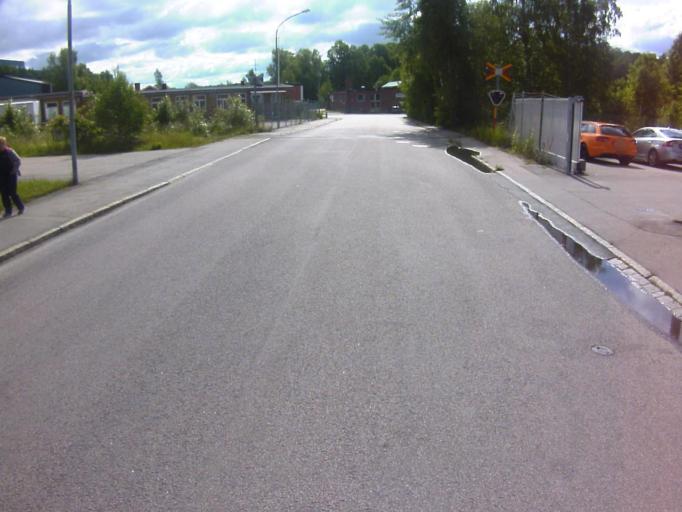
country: SE
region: Soedermanland
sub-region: Eskilstuna Kommun
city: Eskilstuna
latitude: 59.3500
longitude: 16.4884
